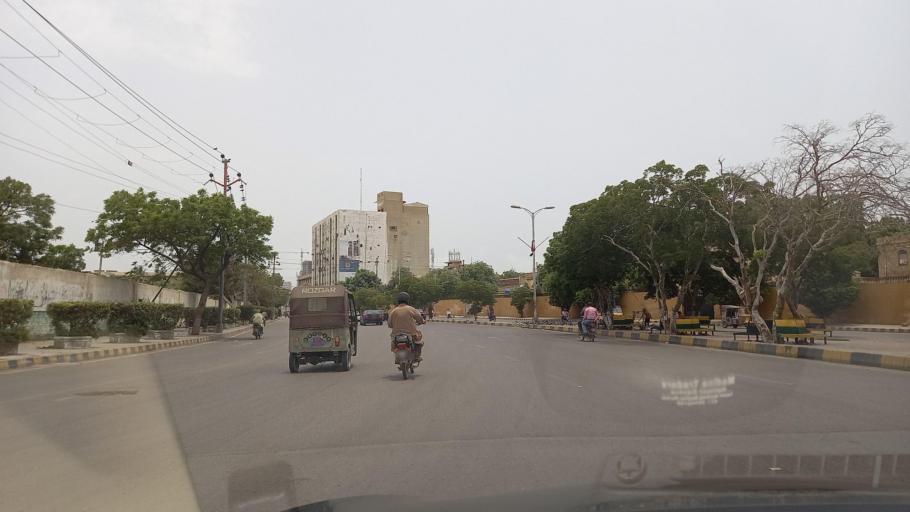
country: PK
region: Sindh
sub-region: Karachi District
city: Karachi
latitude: 24.8536
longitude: 67.0289
